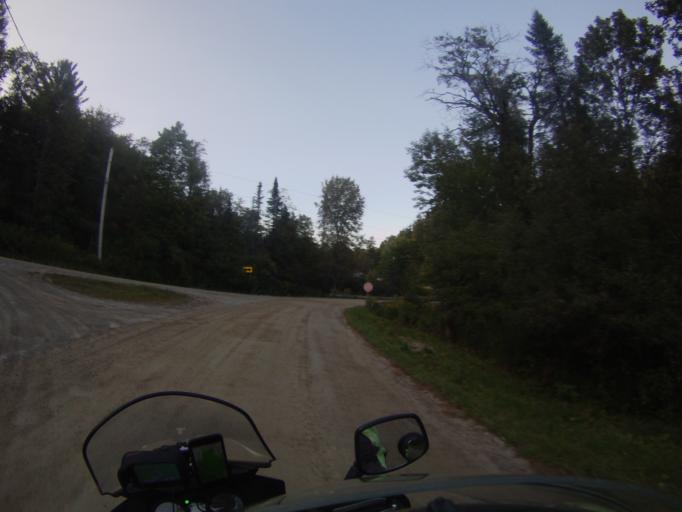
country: US
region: Vermont
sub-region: Addison County
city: Bristol
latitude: 44.0207
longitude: -73.0229
